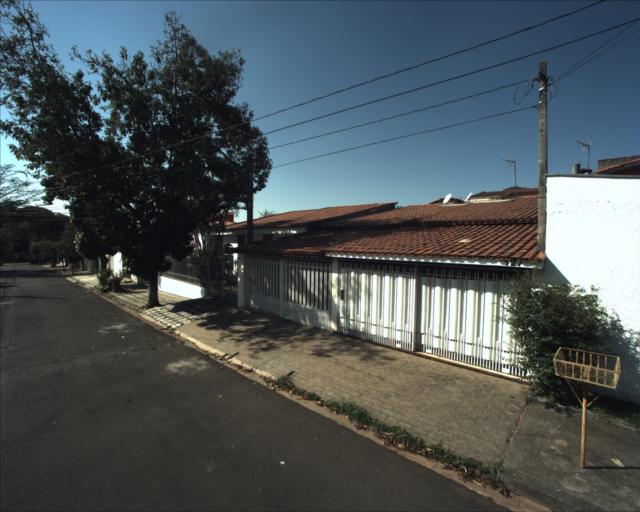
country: BR
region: Sao Paulo
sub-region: Sorocaba
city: Sorocaba
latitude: -23.4949
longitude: -47.4077
